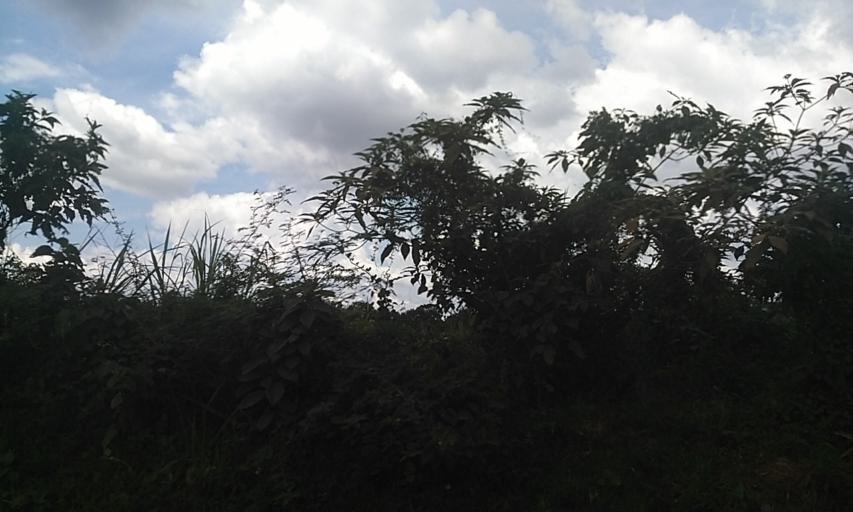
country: UG
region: Central Region
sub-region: Wakiso District
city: Wakiso
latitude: 0.3511
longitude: 32.4754
